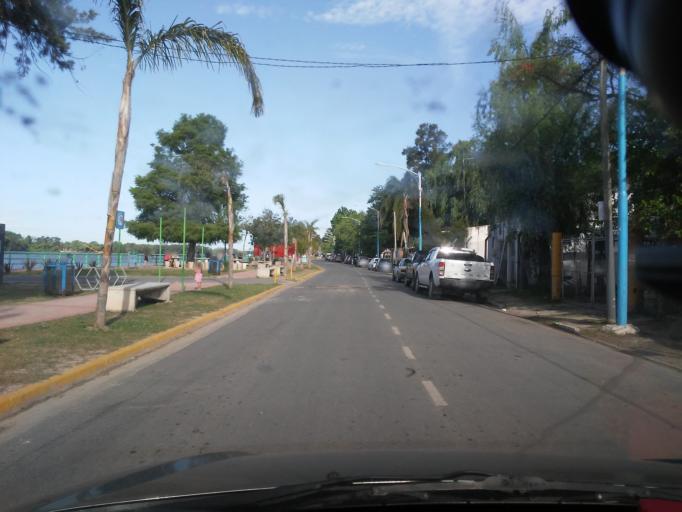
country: AR
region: Buenos Aires
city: Belen de Escobar
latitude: -34.2465
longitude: -58.7343
